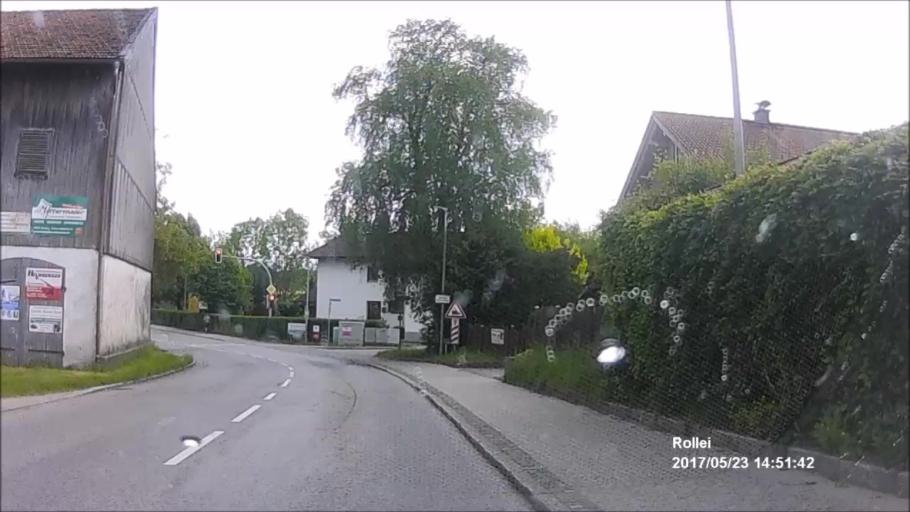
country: DE
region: Bavaria
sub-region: Upper Bavaria
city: Traunreut
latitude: 47.9357
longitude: 12.5939
